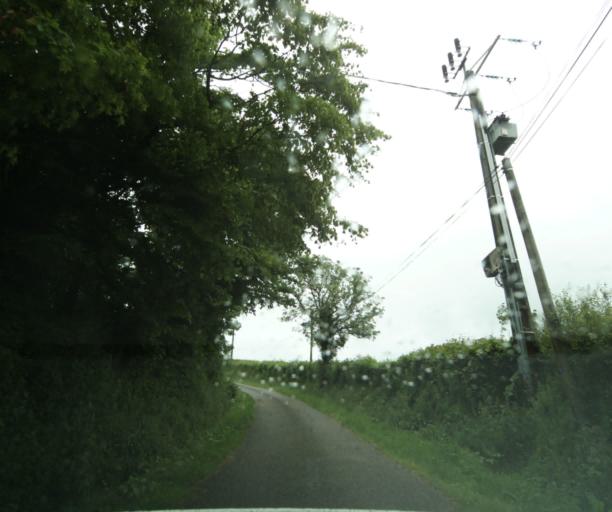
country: FR
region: Bourgogne
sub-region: Departement de Saone-et-Loire
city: Matour
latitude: 46.4858
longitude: 4.4653
